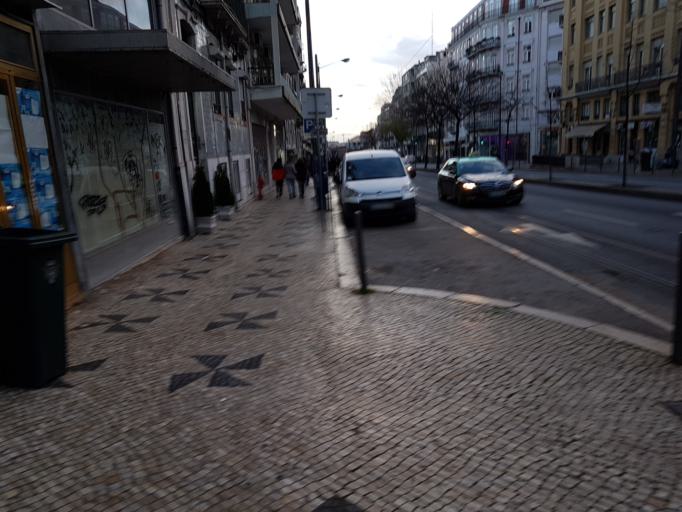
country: PT
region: Lisbon
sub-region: Lisbon
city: Lisbon
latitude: 38.7234
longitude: -9.1351
